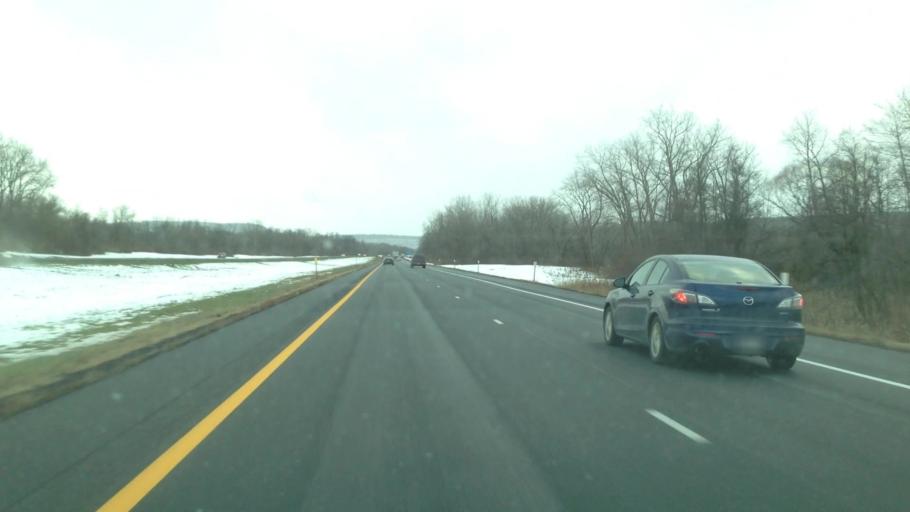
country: US
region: New York
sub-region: Montgomery County
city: Fonda
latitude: 42.9332
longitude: -74.4139
